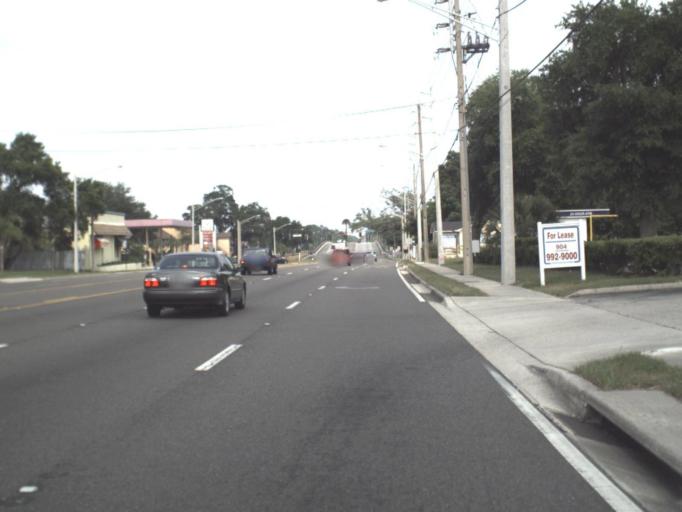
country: US
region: Florida
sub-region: Clay County
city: Bellair-Meadowbrook Terrace
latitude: 30.2474
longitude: -81.7159
